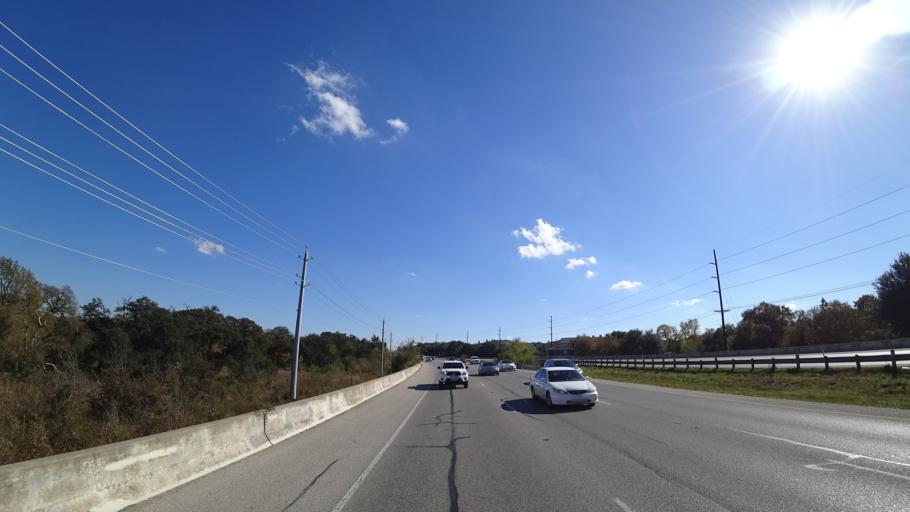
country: US
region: Texas
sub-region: Williamson County
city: Jollyville
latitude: 30.4534
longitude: -97.7512
